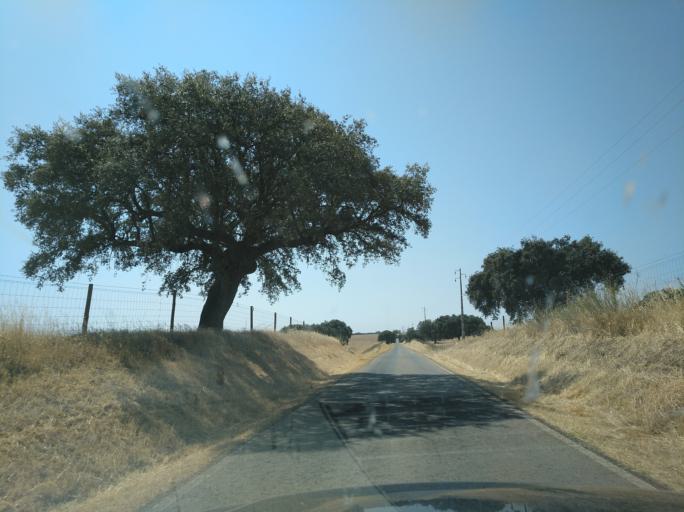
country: PT
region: Portalegre
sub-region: Campo Maior
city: Campo Maior
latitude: 39.0151
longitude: -6.9827
